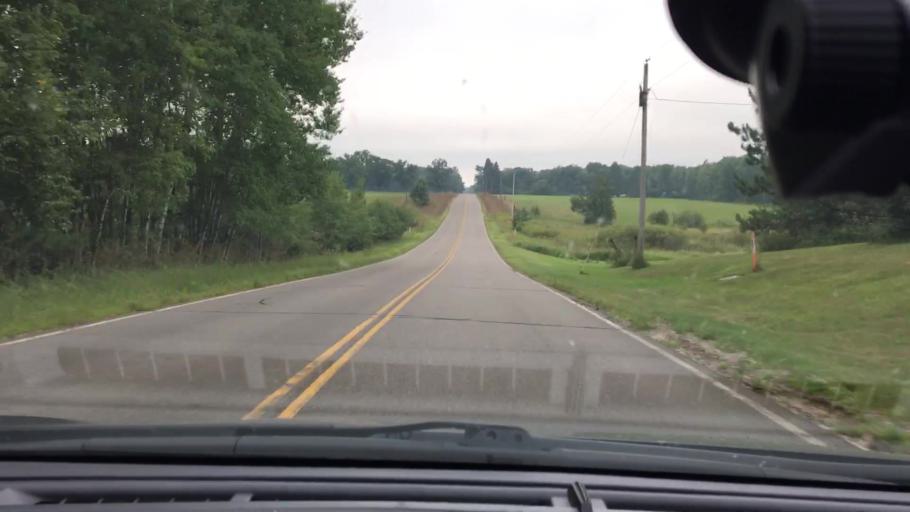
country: US
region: Minnesota
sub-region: Crow Wing County
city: Cross Lake
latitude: 46.6487
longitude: -94.0095
